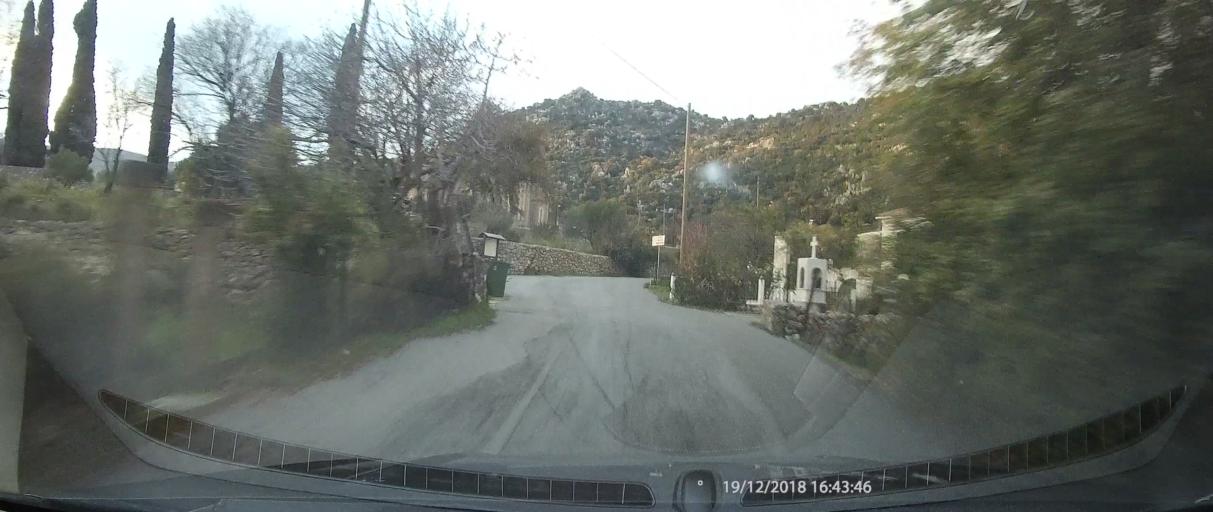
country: GR
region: Peloponnese
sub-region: Nomos Lakonias
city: Sykea
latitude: 36.9146
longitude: 22.9962
